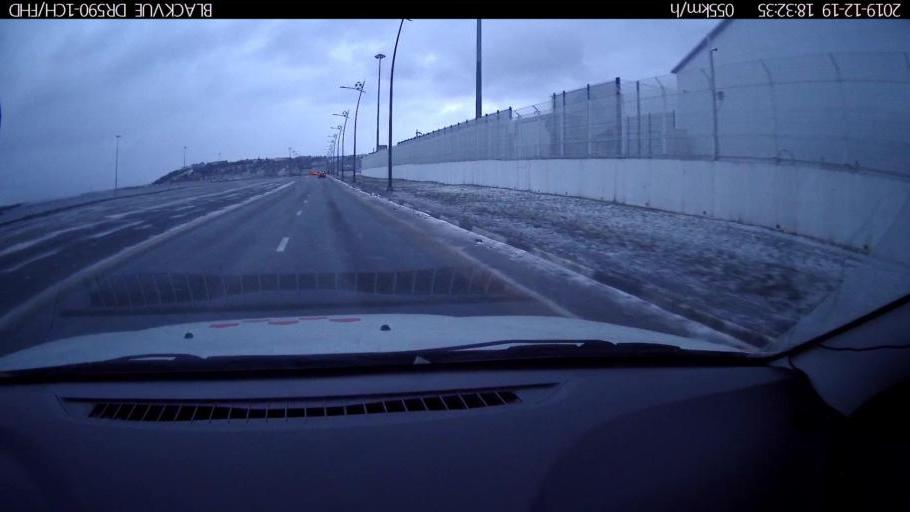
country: RU
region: Nizjnij Novgorod
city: Nizhniy Novgorod
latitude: 56.3370
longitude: 43.9707
